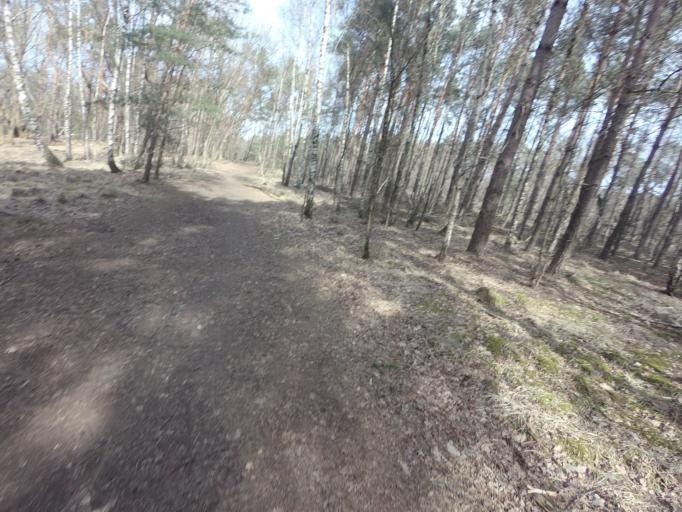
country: NL
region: Limburg
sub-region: Gemeente Roerdalen
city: Vlodrop
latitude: 51.1587
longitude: 6.1025
